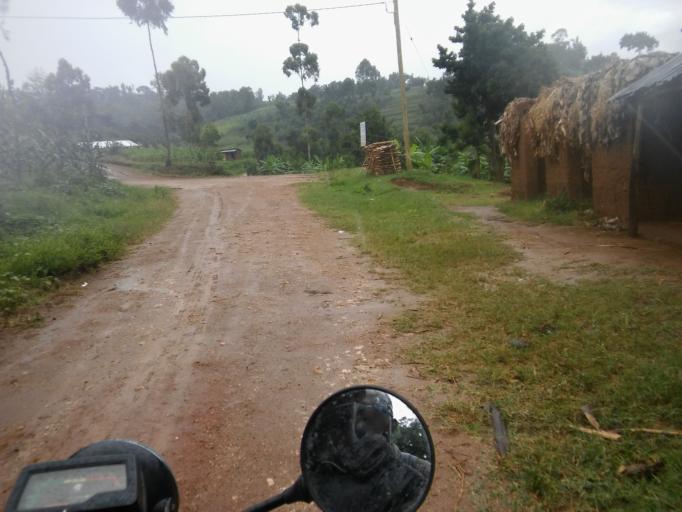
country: UG
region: Eastern Region
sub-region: Bududa District
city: Bududa
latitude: 0.9996
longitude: 34.2474
